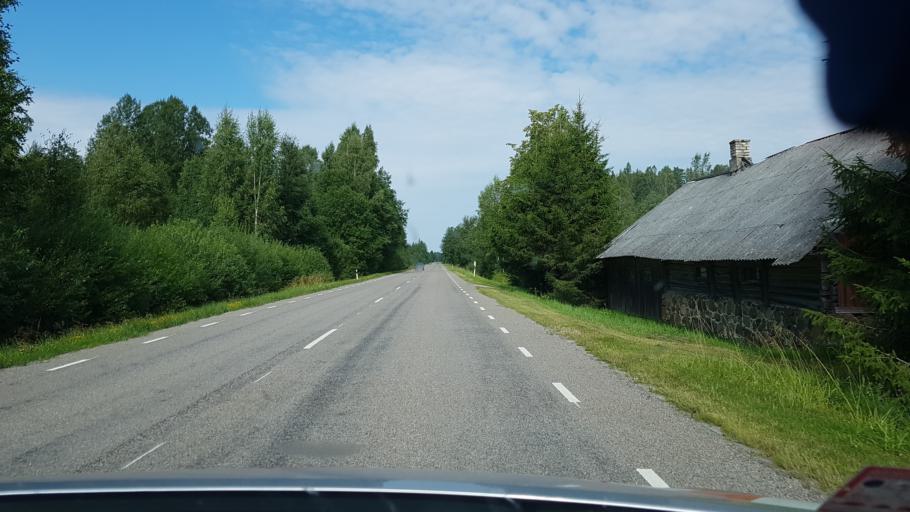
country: EE
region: Raplamaa
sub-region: Jaervakandi vald
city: Jarvakandi
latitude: 58.8061
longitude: 24.8103
